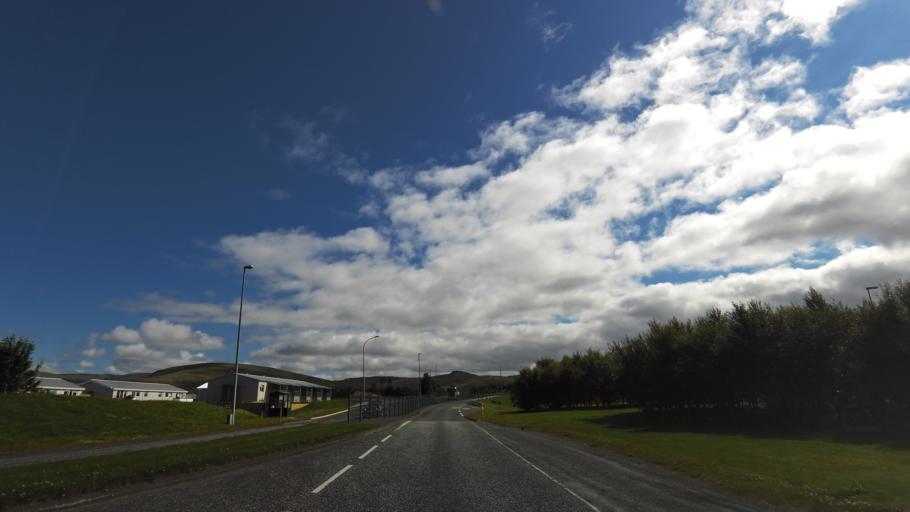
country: IS
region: Capital Region
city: Mosfellsbaer
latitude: 64.1648
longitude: -21.6912
